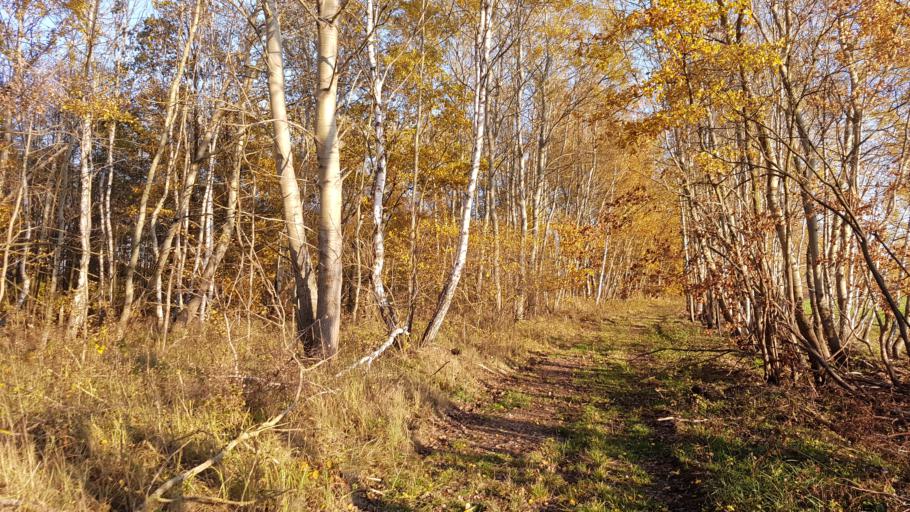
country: DE
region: Brandenburg
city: Schilda
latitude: 51.5934
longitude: 13.3988
